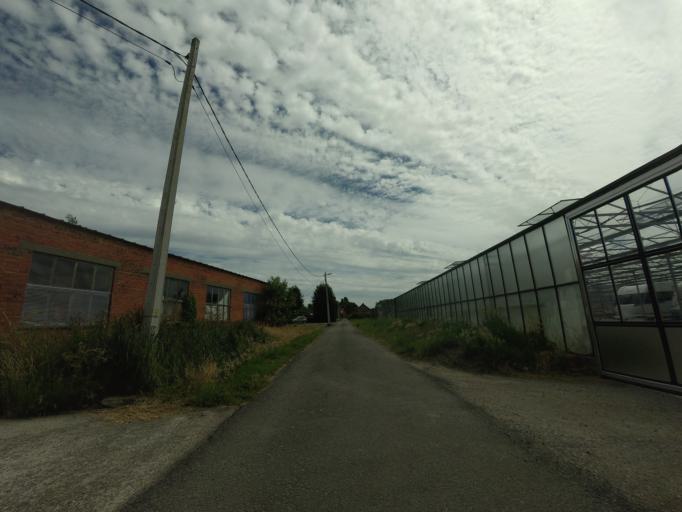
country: BE
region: Flanders
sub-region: Provincie Antwerpen
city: Rumst
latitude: 51.0817
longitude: 4.4622
